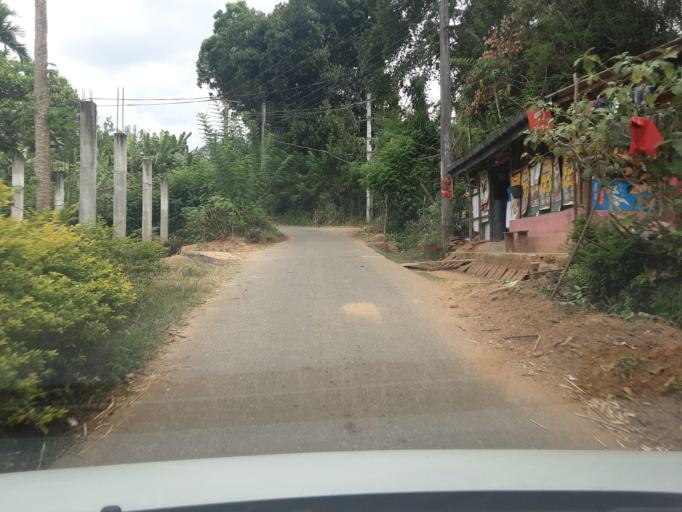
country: LK
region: Uva
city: Badulla
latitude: 7.0860
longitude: 80.9350
